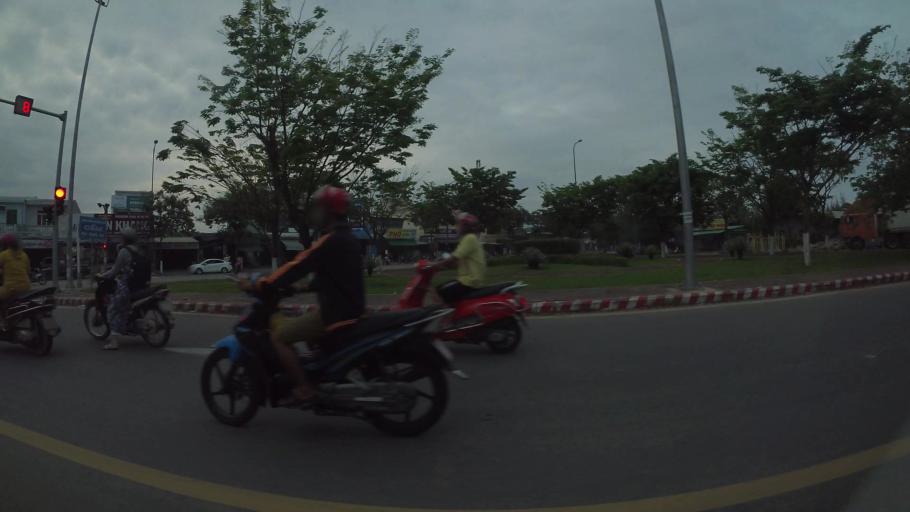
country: VN
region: Da Nang
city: Lien Chieu
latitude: 16.0767
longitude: 108.1139
